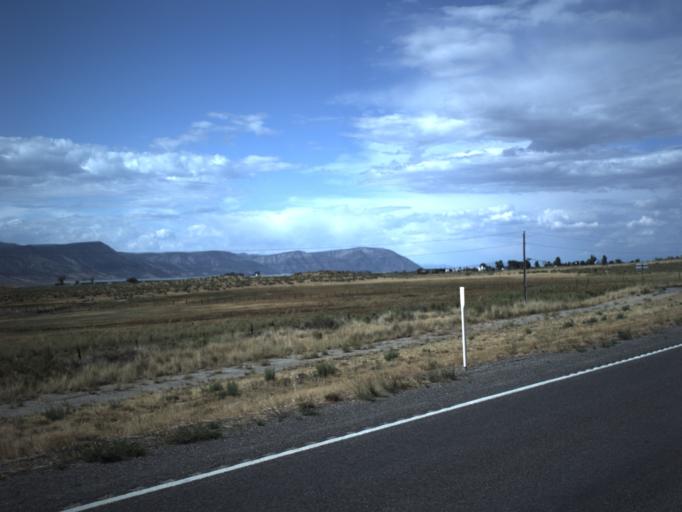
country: US
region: Utah
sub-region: Sanpete County
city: Manti
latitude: 39.2382
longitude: -111.6580
